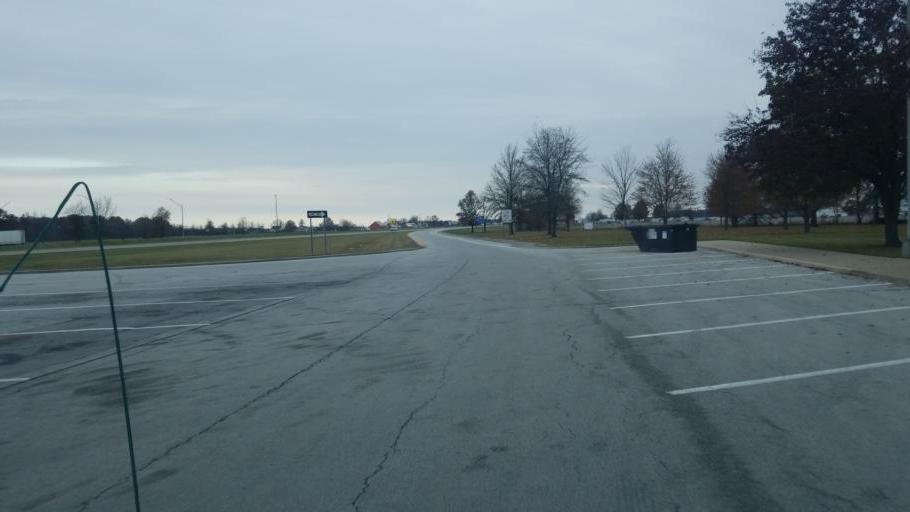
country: US
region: Ohio
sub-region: Auglaize County
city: Saint Marys
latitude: 40.5584
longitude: -84.3282
